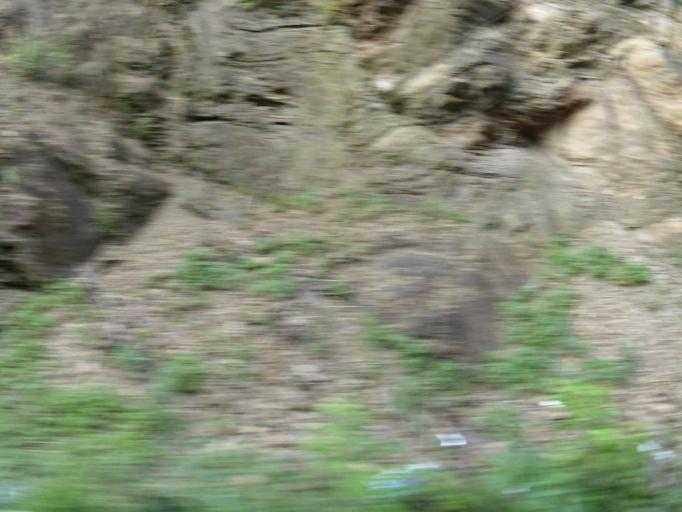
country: US
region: Tennessee
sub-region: Sevier County
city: Seymour
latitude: 35.8871
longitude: -83.7943
